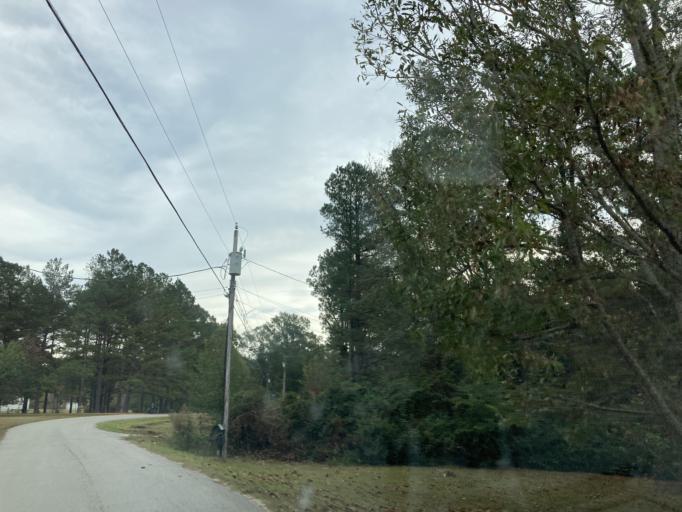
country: US
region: Mississippi
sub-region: Lamar County
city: Purvis
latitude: 31.1587
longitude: -89.4589
